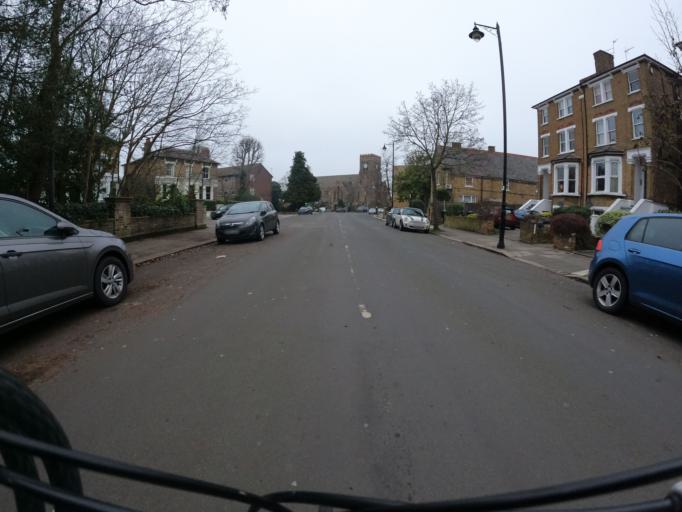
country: GB
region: England
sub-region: Greater London
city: Ealing
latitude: 51.5086
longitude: -0.3164
